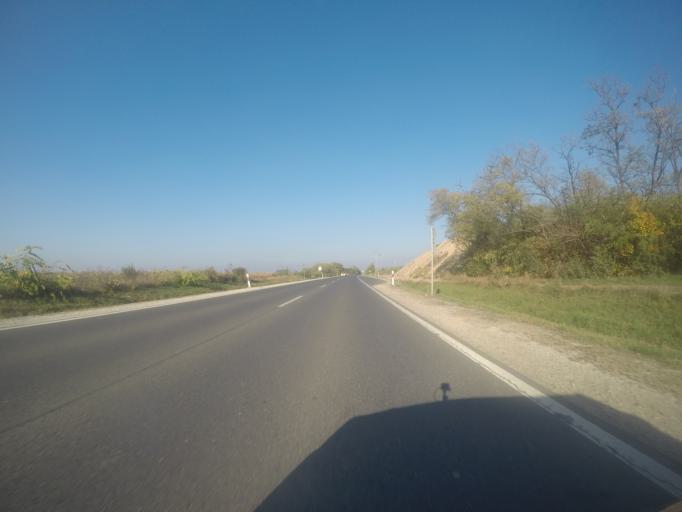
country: HU
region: Fejer
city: Ercsi
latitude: 47.2932
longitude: 18.8765
